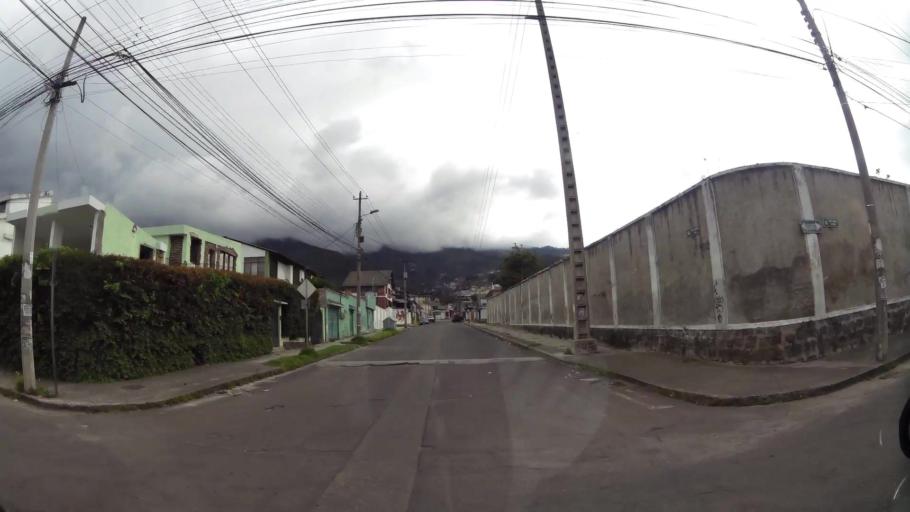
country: EC
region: Pichincha
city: Quito
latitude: -0.1406
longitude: -78.4951
